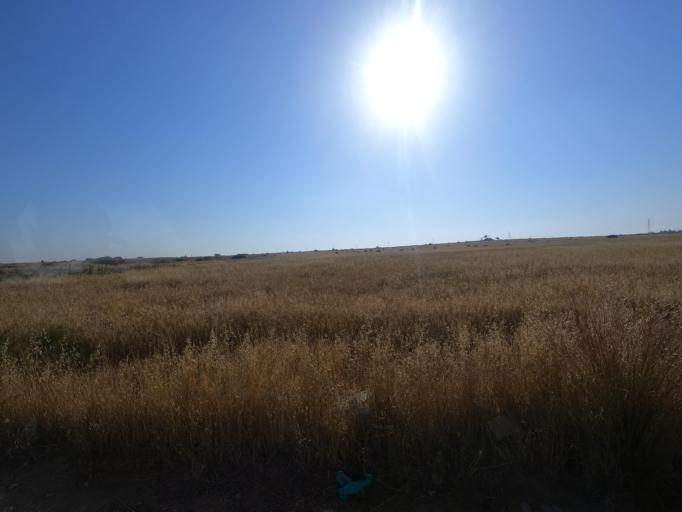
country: CY
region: Ammochostos
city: Frenaros
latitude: 35.0732
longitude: 33.8993
